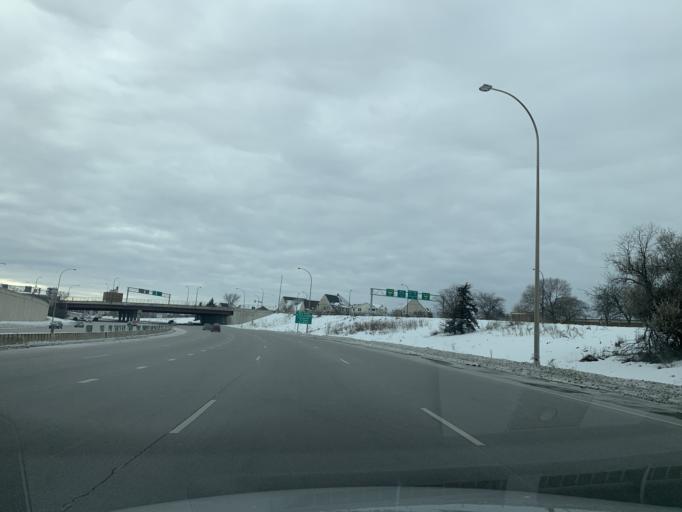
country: US
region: Minnesota
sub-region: Hennepin County
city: Minneapolis
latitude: 44.9901
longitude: -93.2878
